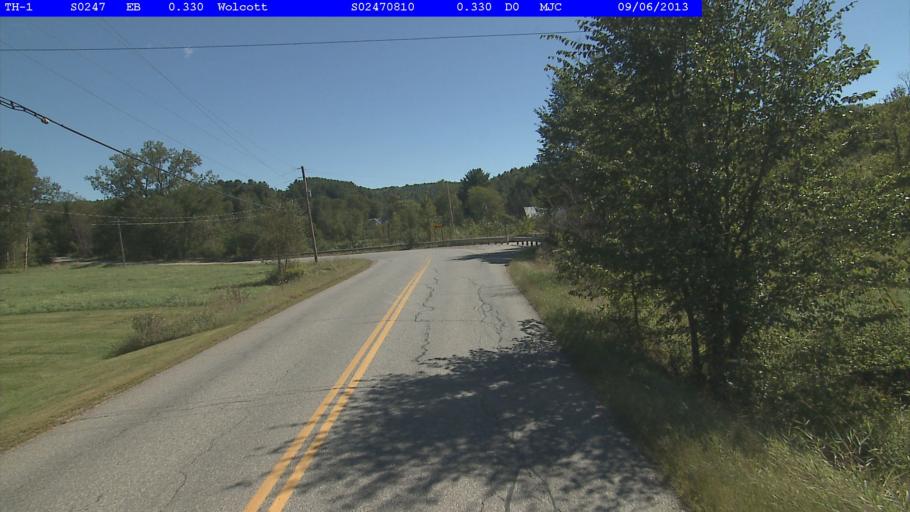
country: US
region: Vermont
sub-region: Lamoille County
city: Morrisville
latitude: 44.5639
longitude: -72.4884
